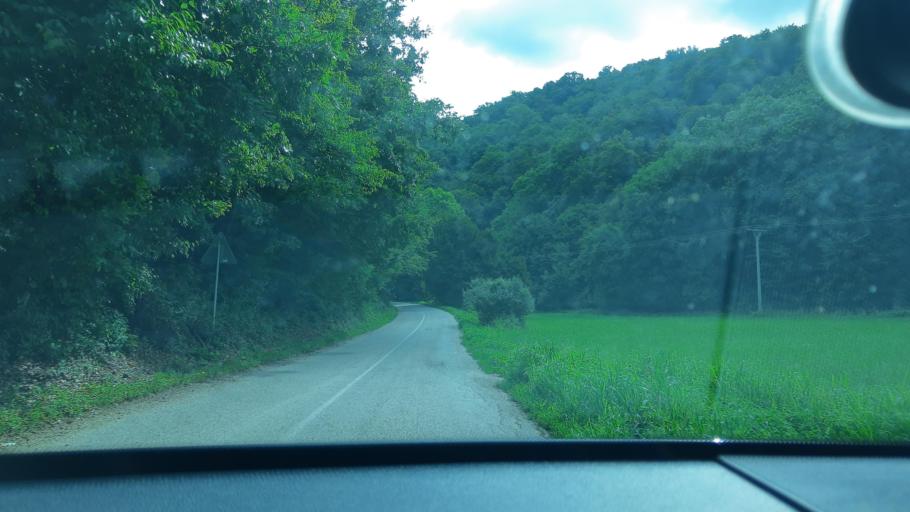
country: SK
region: Trnavsky
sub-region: Okres Trnava
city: Piestany
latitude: 48.6360
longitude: 17.9244
